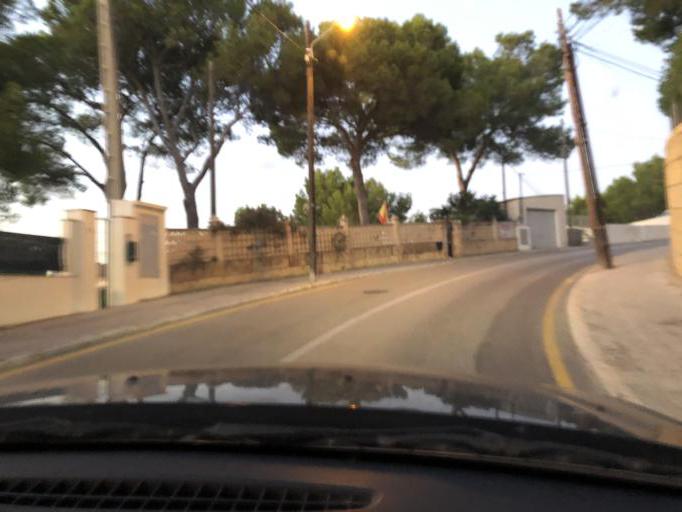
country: ES
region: Balearic Islands
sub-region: Illes Balears
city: Santa Ponsa
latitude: 39.5212
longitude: 2.4734
